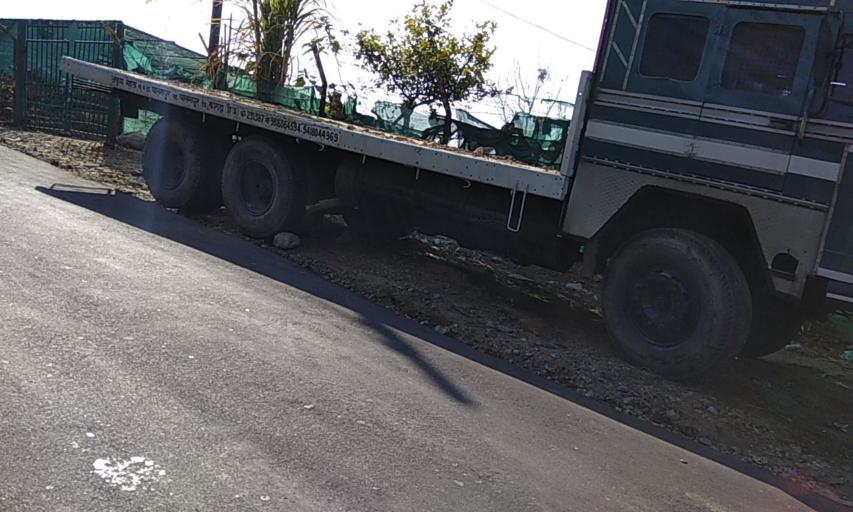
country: IN
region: Himachal Pradesh
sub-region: Kangra
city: Palampur
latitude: 32.1188
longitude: 76.5251
